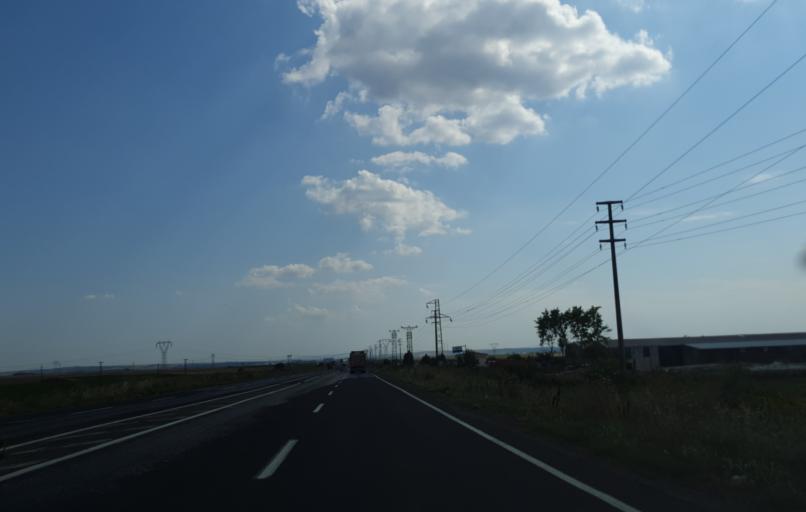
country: TR
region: Kirklareli
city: Buyukkaristiran
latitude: 41.2465
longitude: 27.5402
